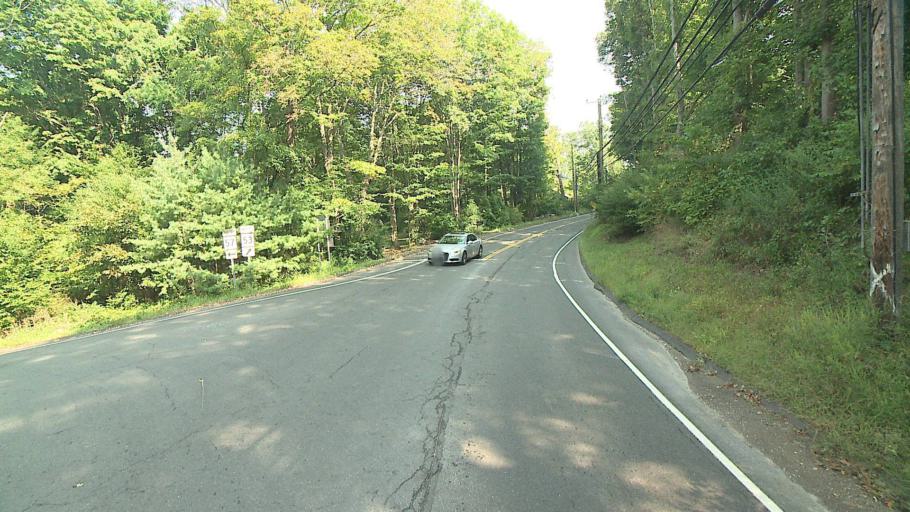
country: US
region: Connecticut
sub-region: Fairfield County
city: Wilton
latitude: 41.2116
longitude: -73.3871
